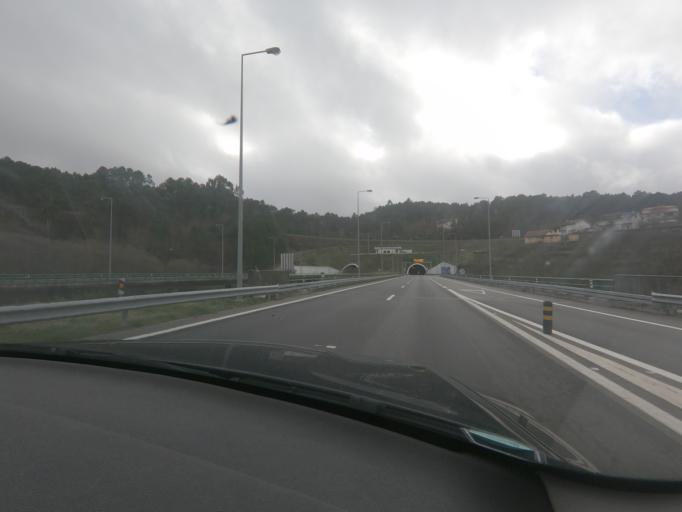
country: PT
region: Viseu
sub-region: Castro Daire
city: Castro Daire
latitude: 40.9000
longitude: -7.9134
